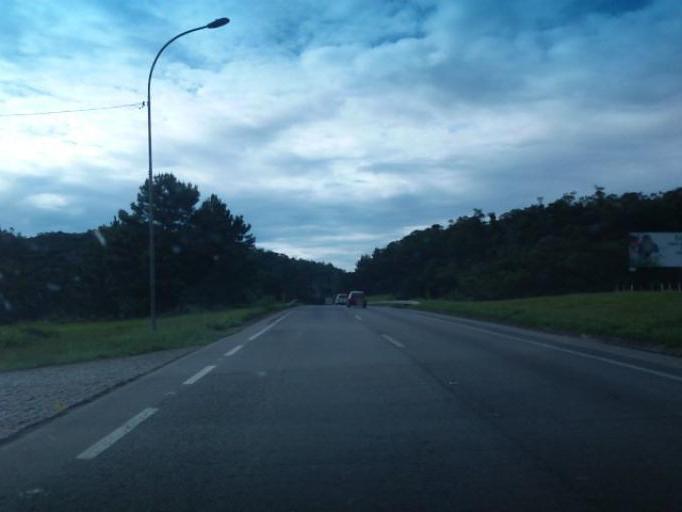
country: BR
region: Parana
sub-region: Campina Grande Do Sul
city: Campina Grande do Sul
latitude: -25.1054
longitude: -48.8058
